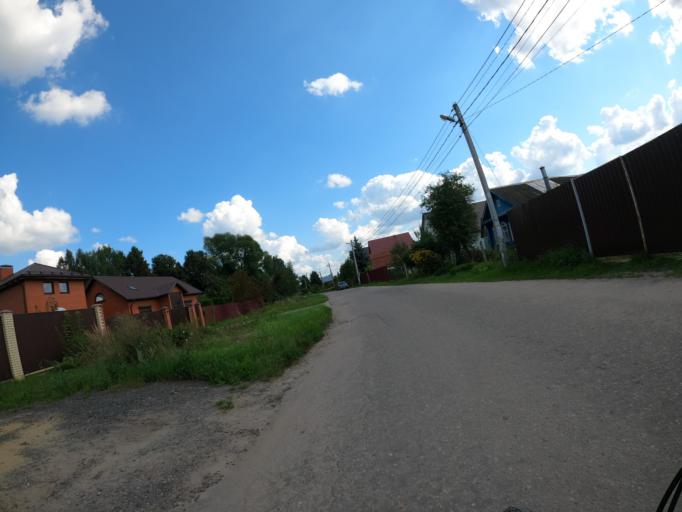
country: RU
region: Moskovskaya
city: Voskresensk
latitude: 55.2734
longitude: 38.6461
